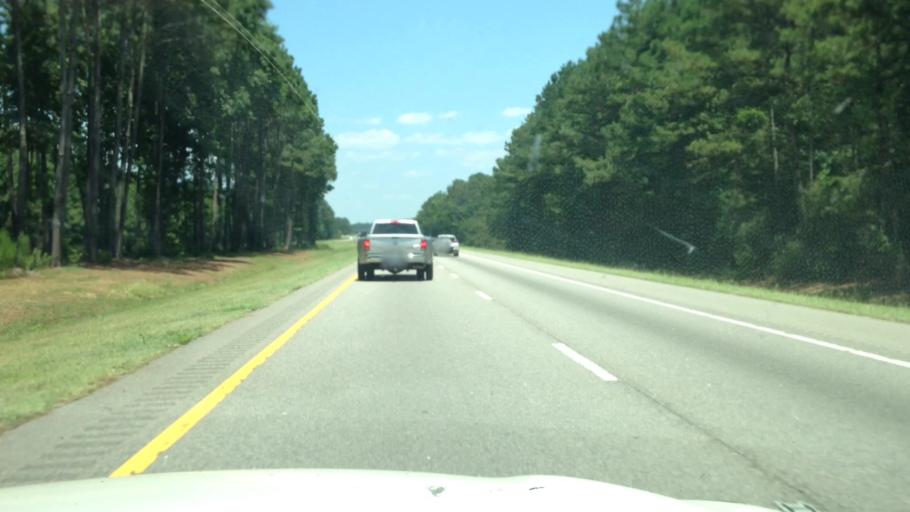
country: US
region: North Carolina
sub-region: Robeson County
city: Rowland
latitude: 34.5473
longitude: -79.2117
